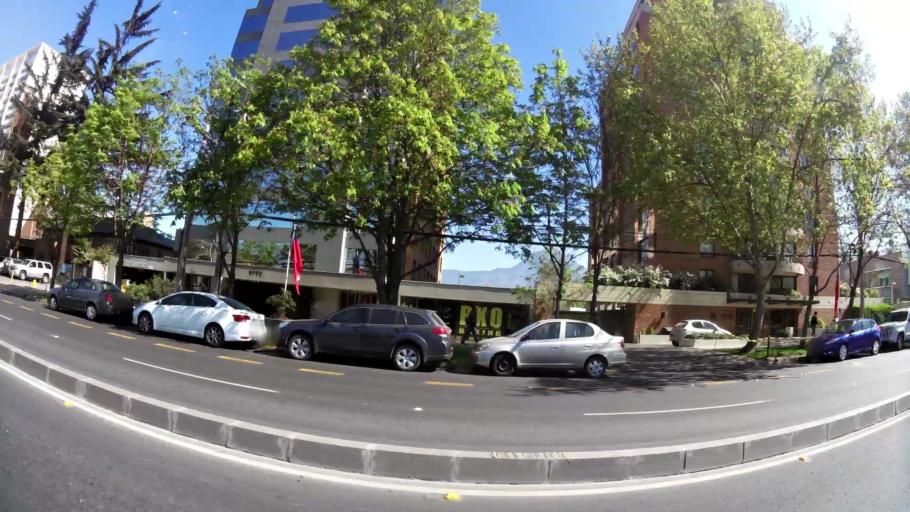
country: CL
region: Santiago Metropolitan
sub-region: Provincia de Santiago
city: Villa Presidente Frei, Nunoa, Santiago, Chile
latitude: -33.3872
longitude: -70.5386
